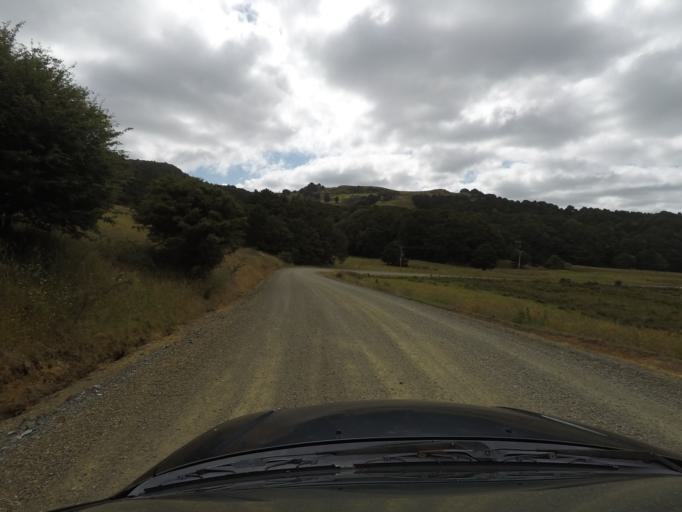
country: NZ
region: Northland
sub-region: Whangarei
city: Ruakaka
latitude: -35.9324
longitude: 174.3458
